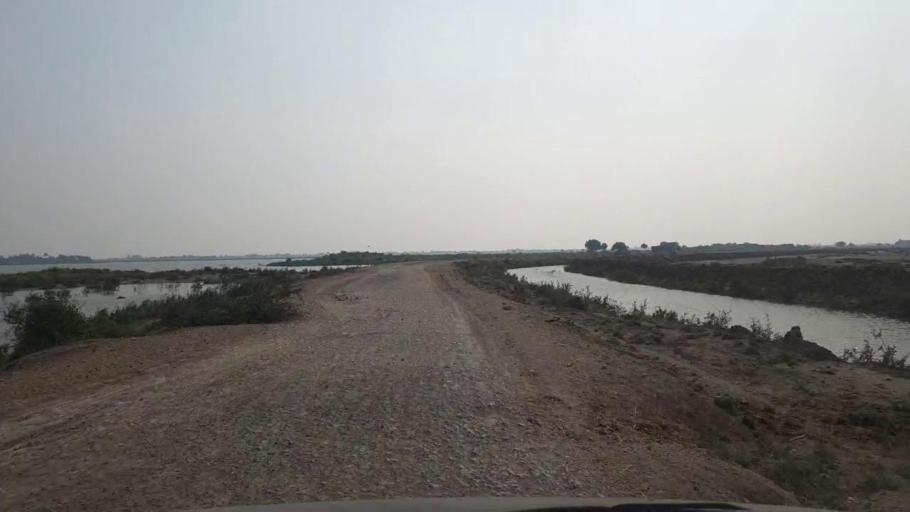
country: PK
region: Sindh
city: Tando Muhammad Khan
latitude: 25.0847
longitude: 68.3873
